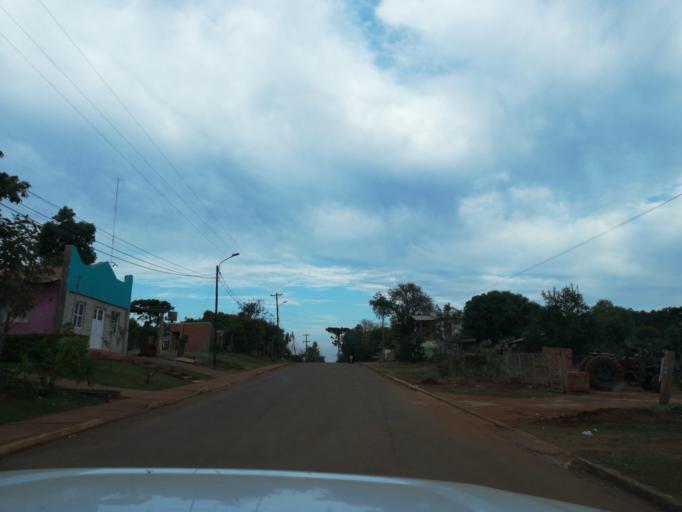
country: AR
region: Misiones
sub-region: Departamento de San Pedro
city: San Pedro
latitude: -26.6238
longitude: -54.0979
